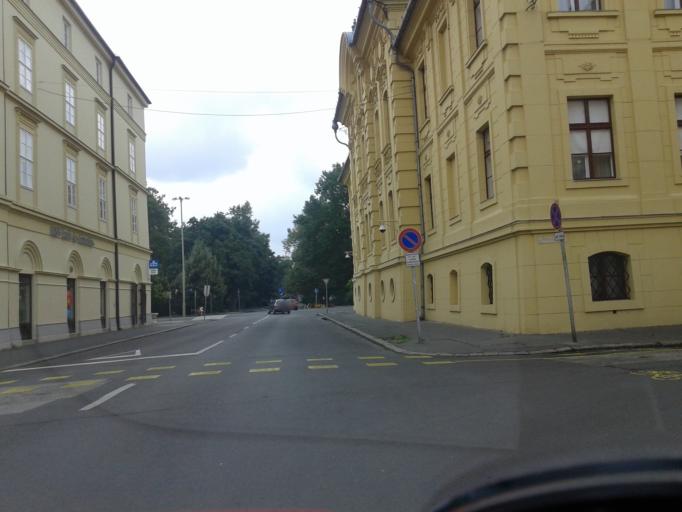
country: HU
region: Csongrad
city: Szeged
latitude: 46.2548
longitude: 20.1478
